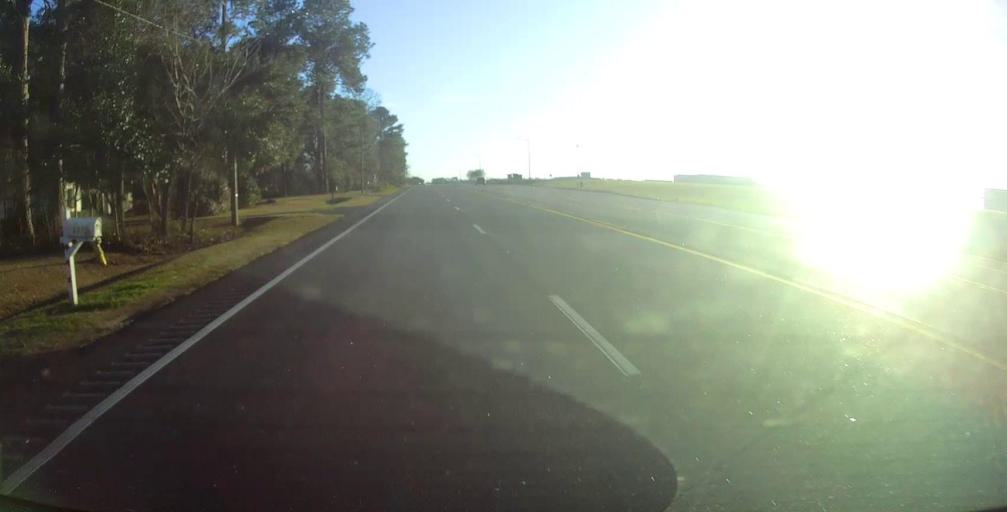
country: US
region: Georgia
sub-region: Dougherty County
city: Albany
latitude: 31.5374
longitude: -84.1832
